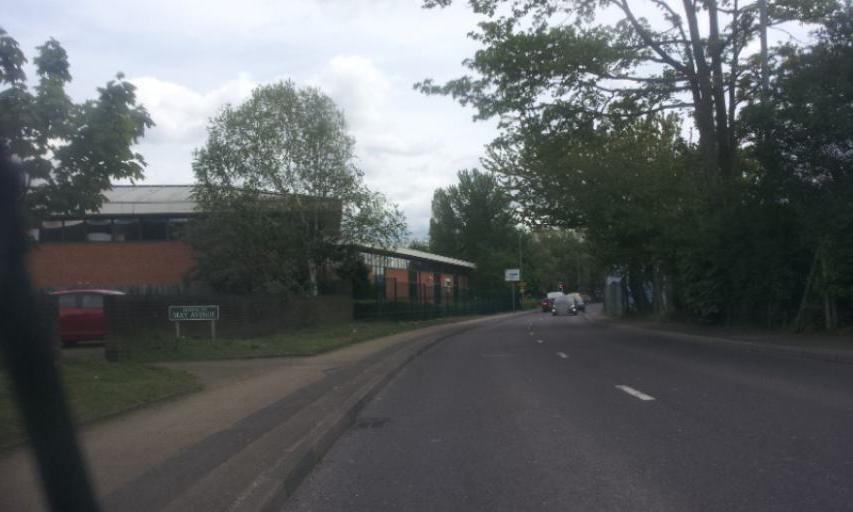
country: GB
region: England
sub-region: Greater London
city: Orpington
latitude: 51.3887
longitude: 0.1076
